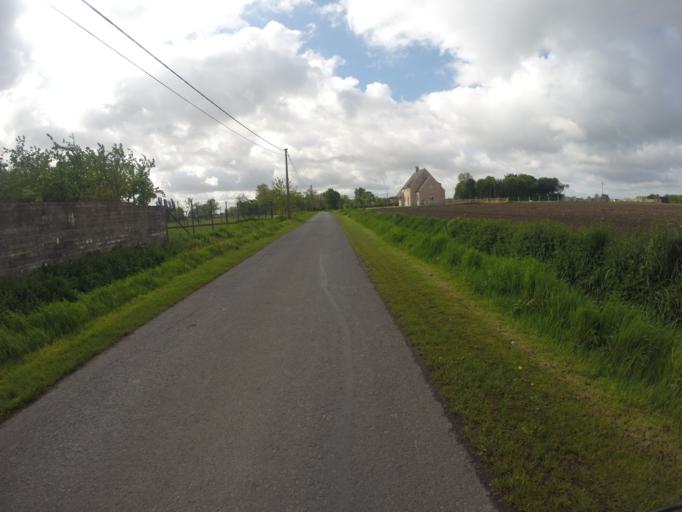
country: BE
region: Flanders
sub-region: Provincie West-Vlaanderen
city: Ruiselede
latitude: 51.0619
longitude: 3.3863
